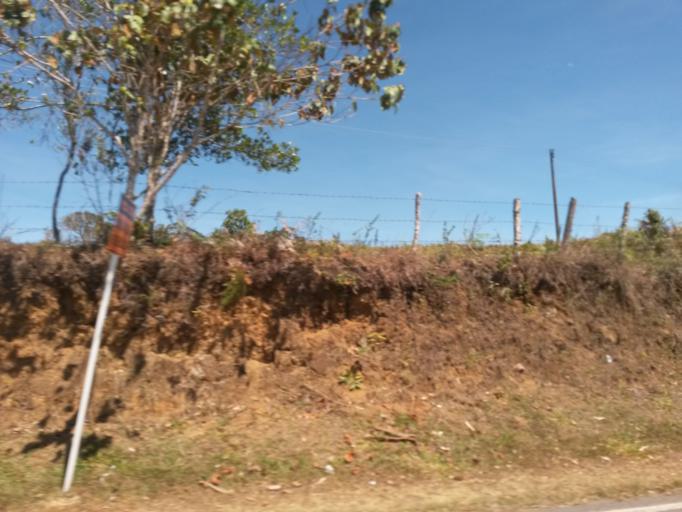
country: CO
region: Cauca
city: Lopez
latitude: 2.4444
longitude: -76.7917
